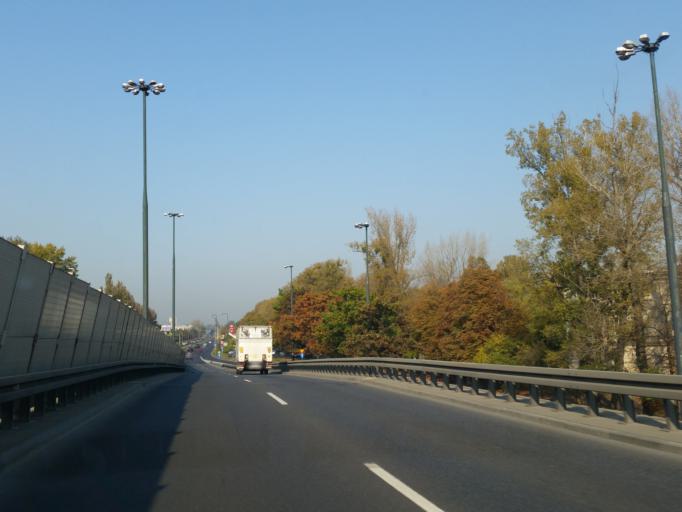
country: PL
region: Masovian Voivodeship
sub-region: Warszawa
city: Wlochy
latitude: 52.1836
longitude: 20.9785
